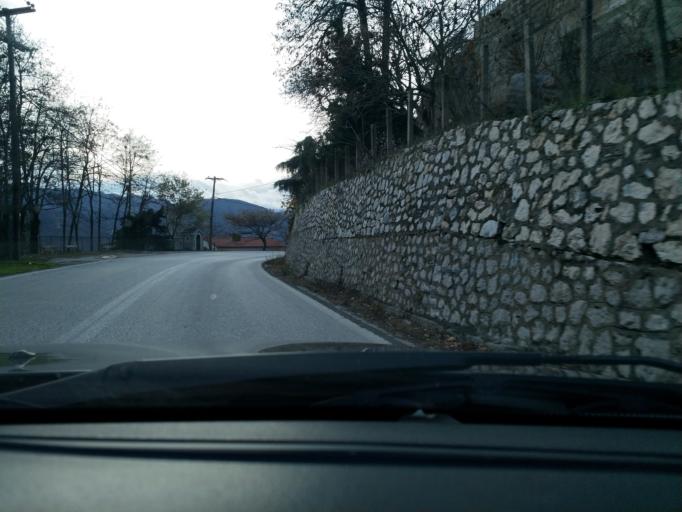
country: GR
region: Thessaly
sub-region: Trikala
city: Kastraki
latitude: 39.7882
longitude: 21.4154
